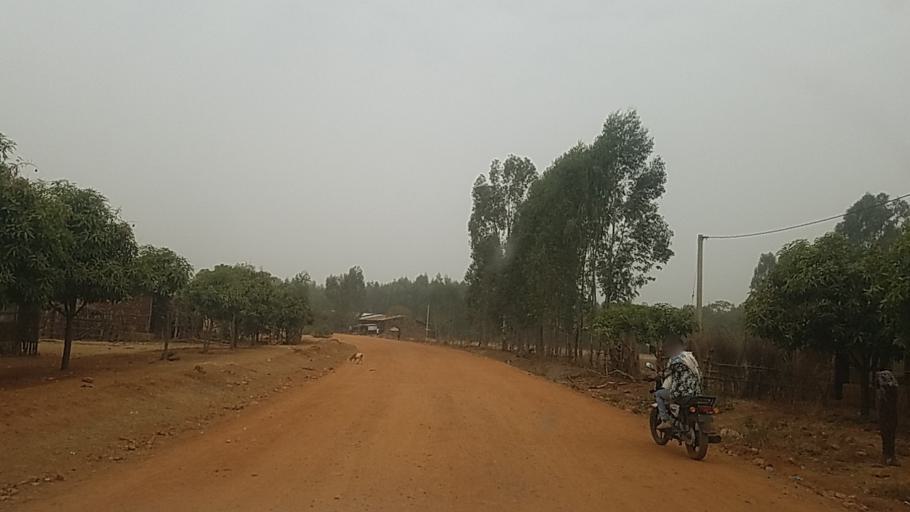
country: ET
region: Amhara
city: Bure
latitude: 10.8790
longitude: 36.4201
